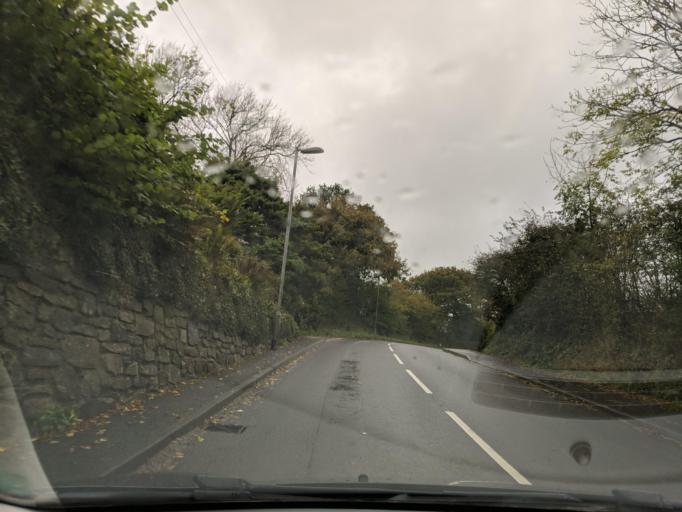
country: GB
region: England
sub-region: Cornwall
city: Bodmin
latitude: 50.4653
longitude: -4.7201
